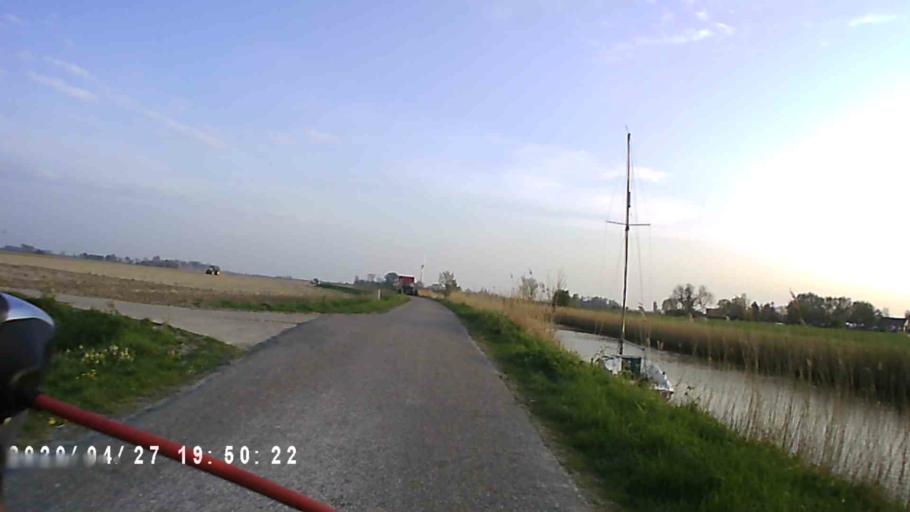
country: NL
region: Groningen
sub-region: Gemeente Zuidhorn
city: Oldehove
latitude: 53.3416
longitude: 6.4312
